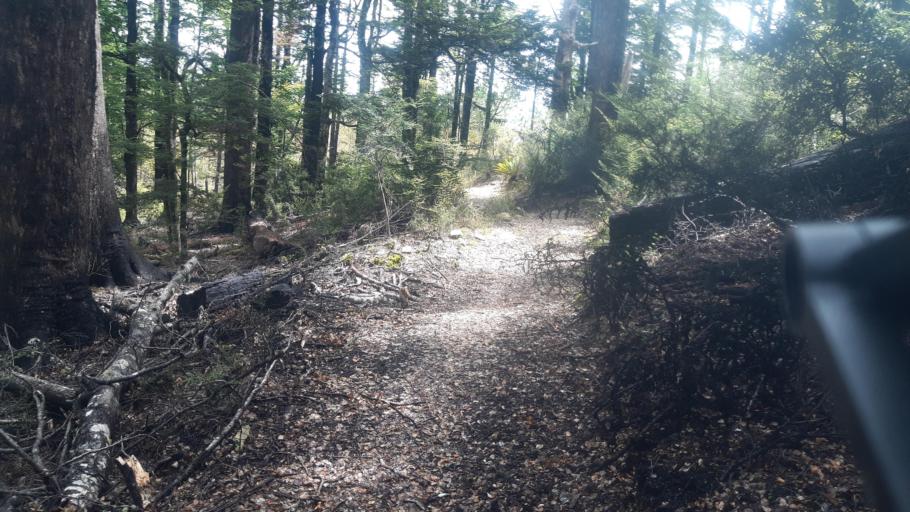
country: NZ
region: Tasman
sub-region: Tasman District
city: Wakefield
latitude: -41.7598
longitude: 172.8045
